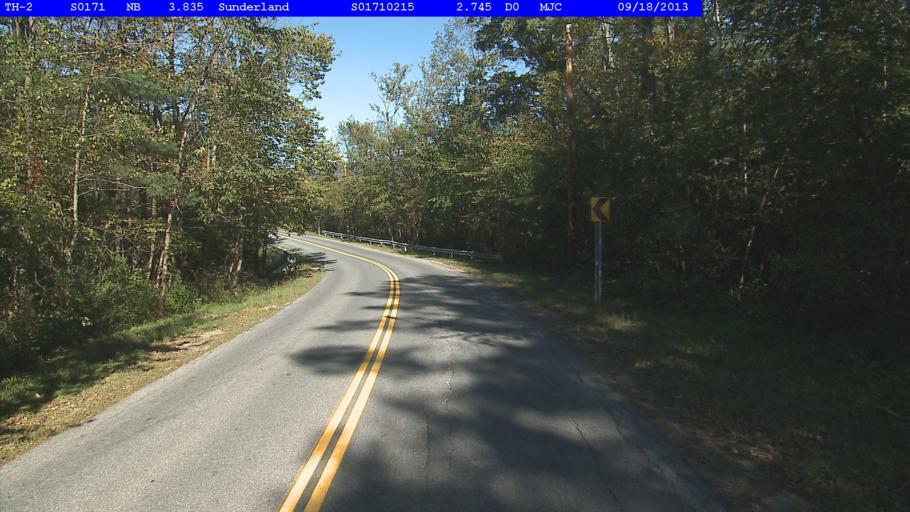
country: US
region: Vermont
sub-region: Bennington County
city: Arlington
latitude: 43.1038
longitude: -73.1221
